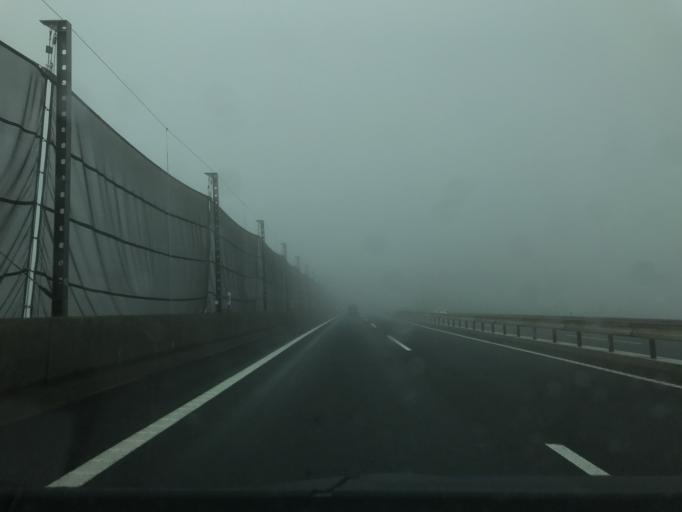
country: JP
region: Oita
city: Beppu
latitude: 33.3245
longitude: 131.4599
